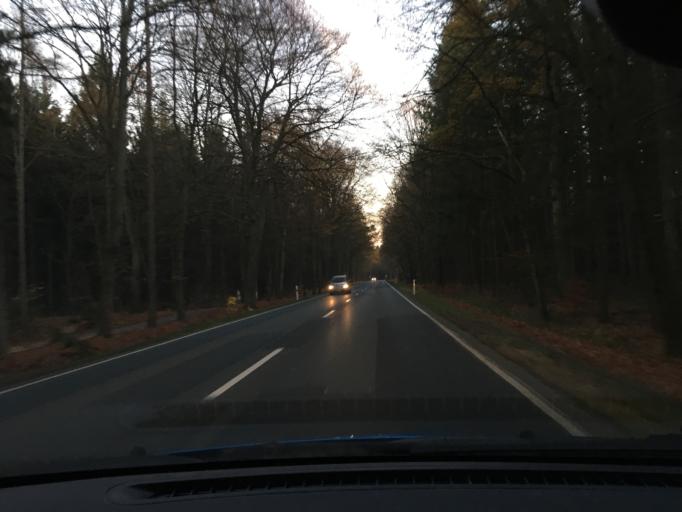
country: DE
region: Lower Saxony
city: Uelzen
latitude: 52.9857
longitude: 10.5151
